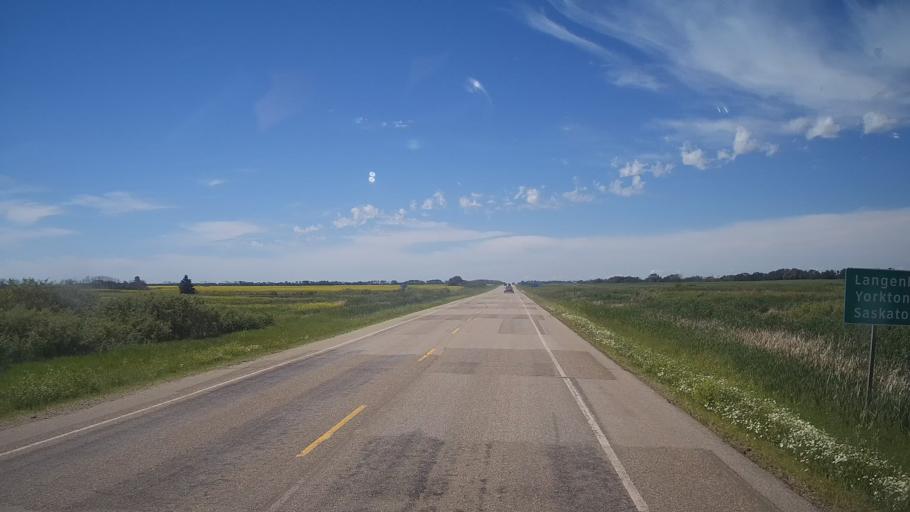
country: CA
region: Saskatchewan
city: Langenburg
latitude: 50.7787
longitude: -101.5131
